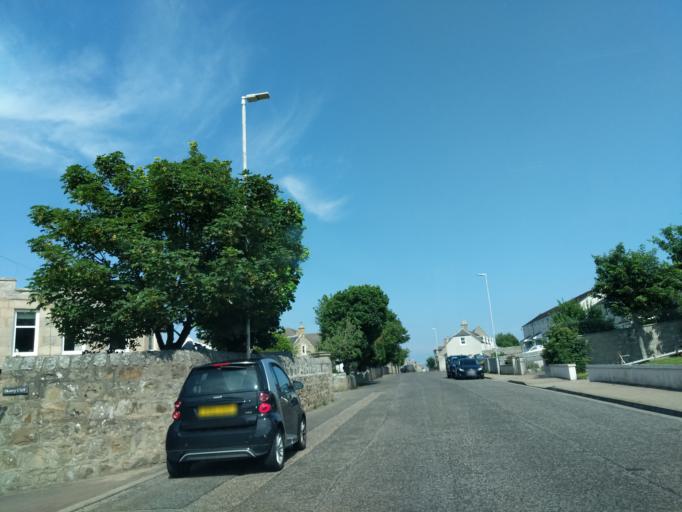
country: GB
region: Scotland
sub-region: Moray
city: Lossiemouth
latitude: 57.7180
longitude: -3.3013
